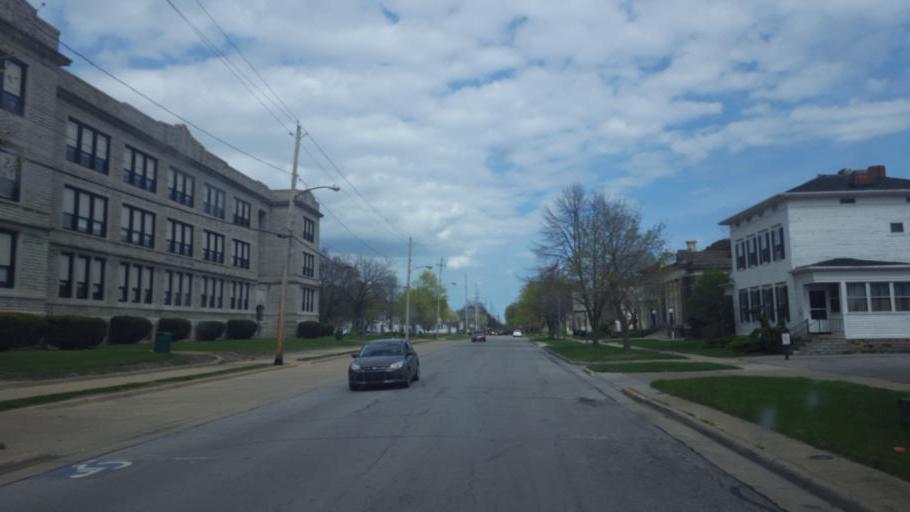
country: US
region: Ohio
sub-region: Erie County
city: Sandusky
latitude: 41.4538
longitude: -82.7100
